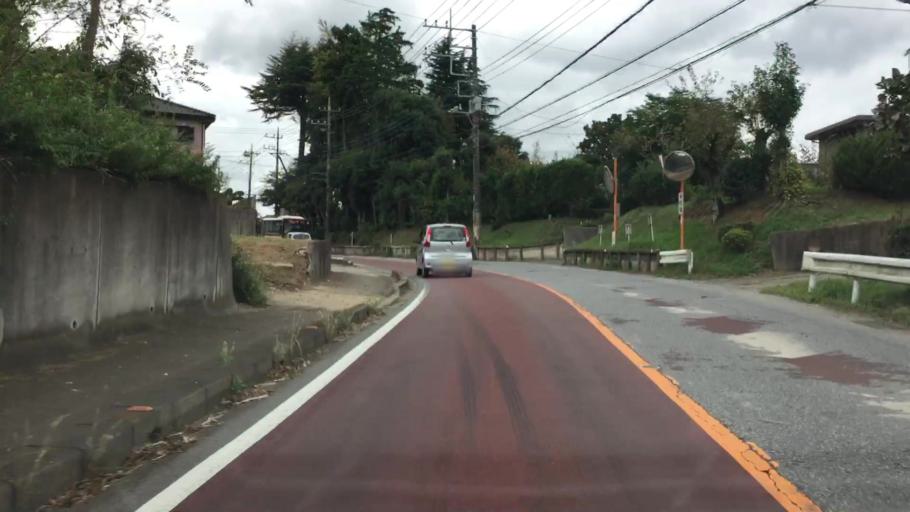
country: JP
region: Chiba
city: Shiroi
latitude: 35.8262
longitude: 140.1390
